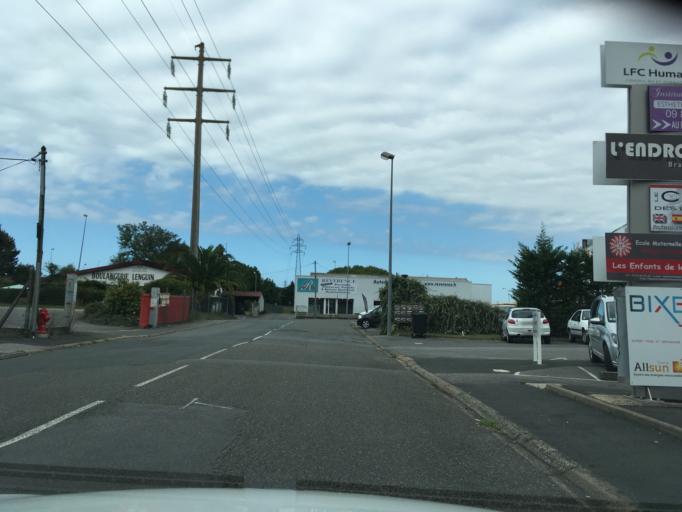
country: FR
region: Aquitaine
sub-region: Departement des Pyrenees-Atlantiques
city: Bayonne
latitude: 43.4958
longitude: -1.4967
